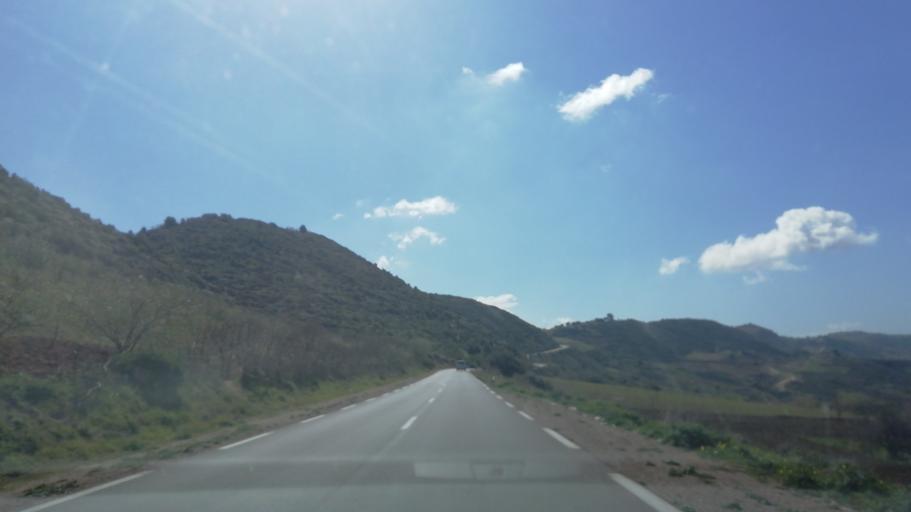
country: DZ
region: Mascara
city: Mascara
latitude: 35.4686
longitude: 0.1539
